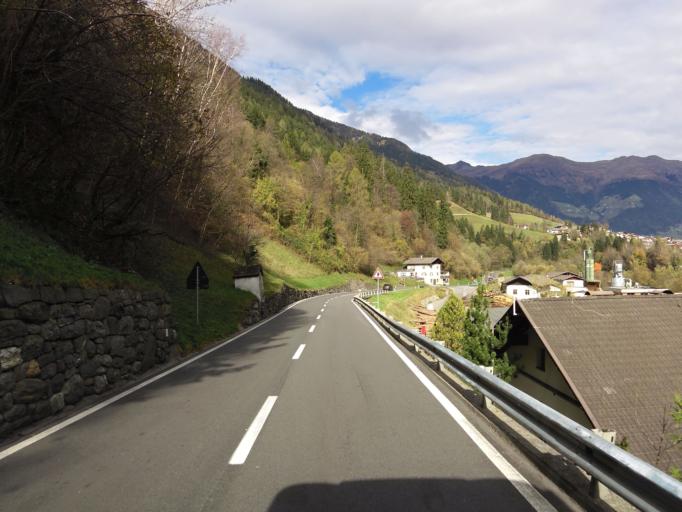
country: IT
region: Trentino-Alto Adige
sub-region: Bolzano
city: San Martino in Passiria
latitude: 46.7707
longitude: 11.2171
